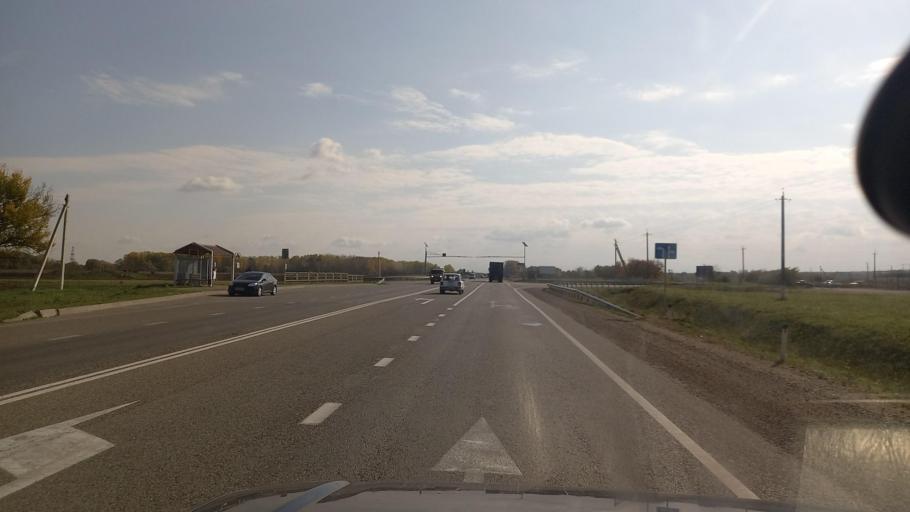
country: RU
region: Krasnodarskiy
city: Novoukrainskiy
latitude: 44.8899
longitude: 38.0737
